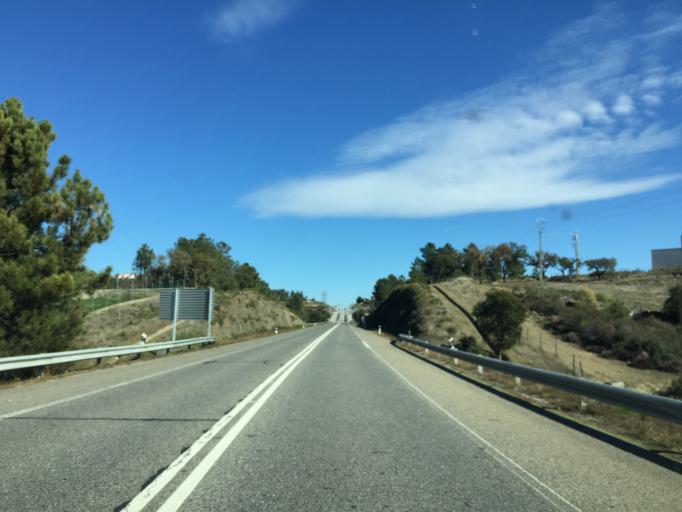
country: PT
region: Castelo Branco
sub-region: Castelo Branco
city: Castelo Branco
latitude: 39.8232
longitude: -7.5168
